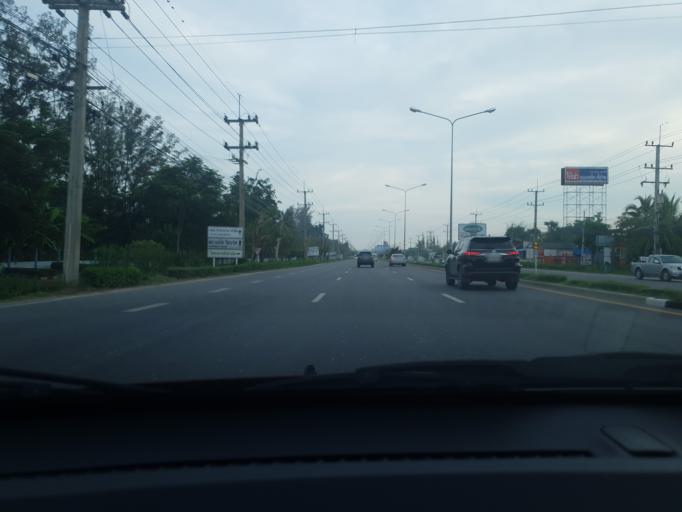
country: TH
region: Prachuap Khiri Khan
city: Hua Hin
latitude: 12.6785
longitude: 99.9527
